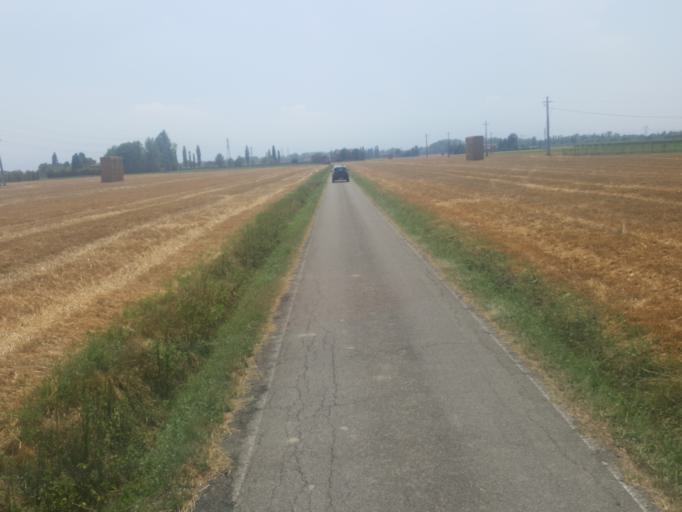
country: IT
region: Emilia-Romagna
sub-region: Provincia di Modena
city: Gaggio
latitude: 44.6458
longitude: 11.0015
